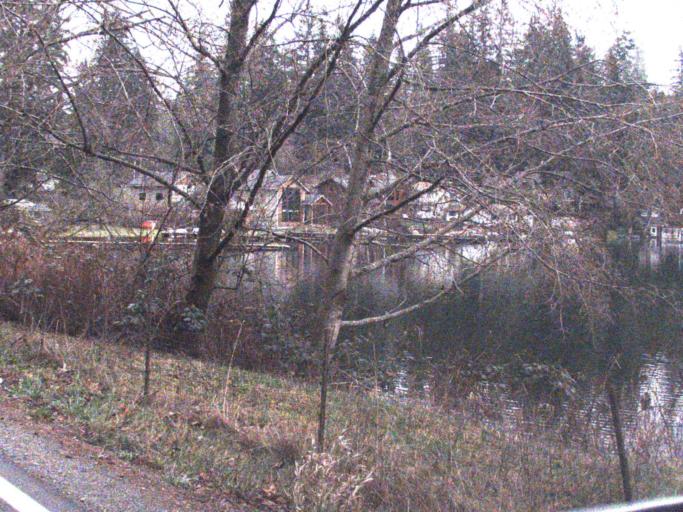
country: US
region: Washington
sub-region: Snohomish County
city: Smokey Point
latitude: 48.1553
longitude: -122.2593
